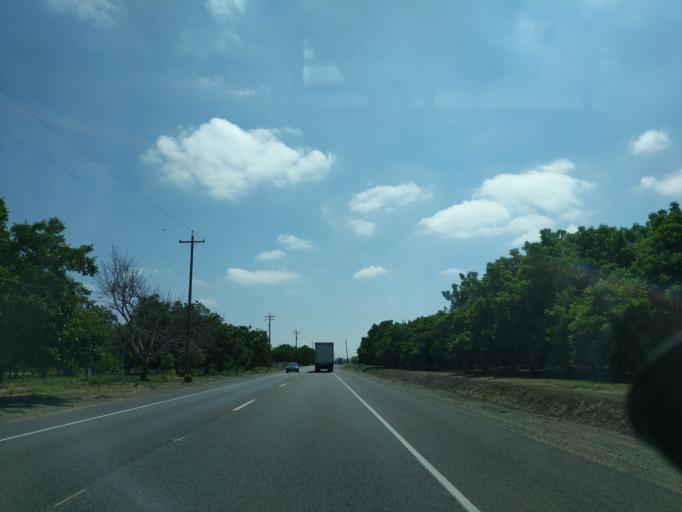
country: US
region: California
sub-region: San Joaquin County
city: Linden
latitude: 37.9345
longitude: -121.0722
